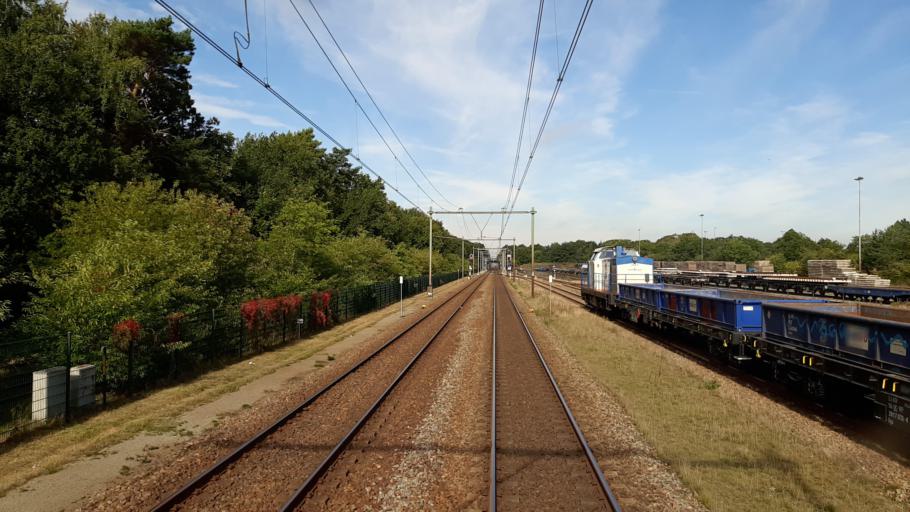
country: NL
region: North Holland
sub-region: Gemeente Bussum
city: Bussum
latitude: 52.2598
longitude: 5.1651
